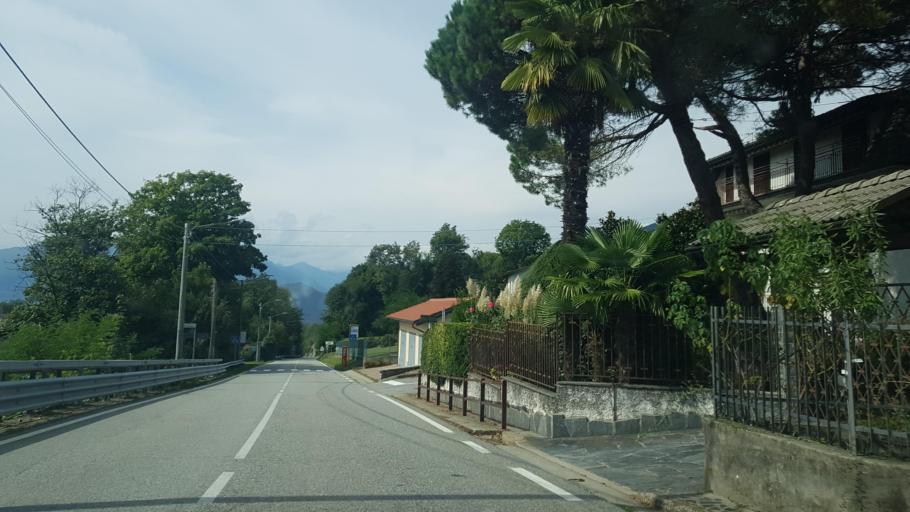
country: IT
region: Piedmont
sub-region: Provincia Verbano-Cusio-Ossola
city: Bee
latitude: 45.9620
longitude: 8.5769
